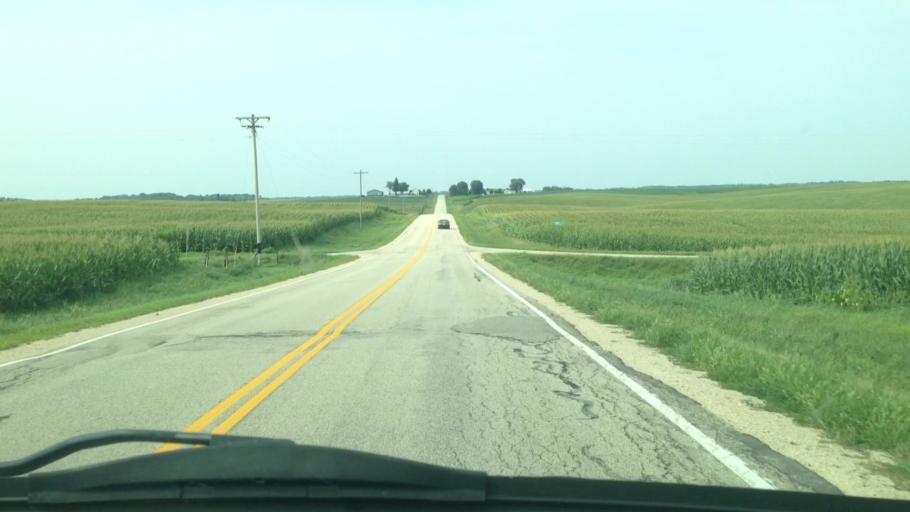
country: US
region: Minnesota
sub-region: Winona County
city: Lewiston
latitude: 43.8824
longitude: -91.9594
